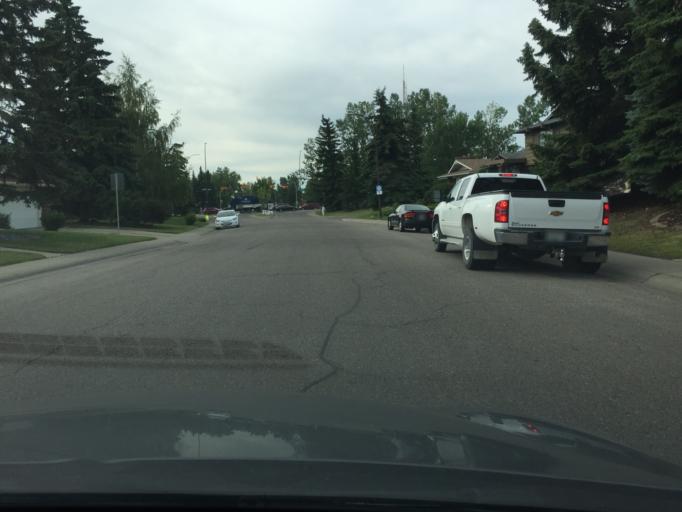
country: CA
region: Alberta
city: Calgary
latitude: 50.9316
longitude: -114.0390
